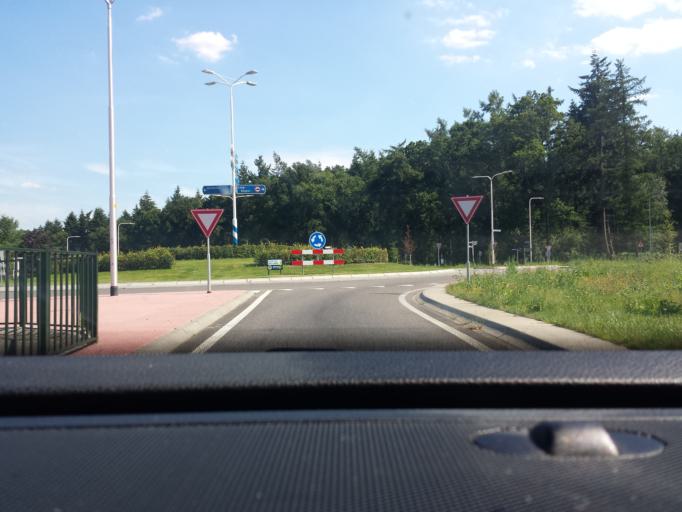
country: NL
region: Gelderland
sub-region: Gemeente Doetinchem
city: Doetinchem
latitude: 52.0012
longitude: 6.2284
